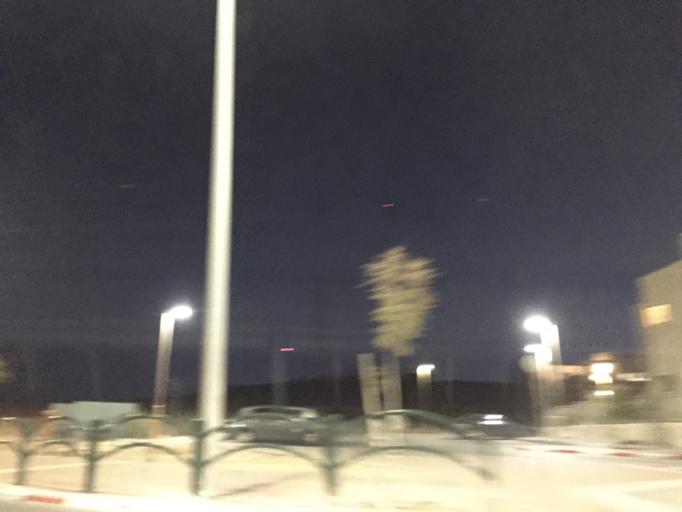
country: IL
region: Southern District
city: Mitzpe Ramon
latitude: 30.6166
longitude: 34.8004
